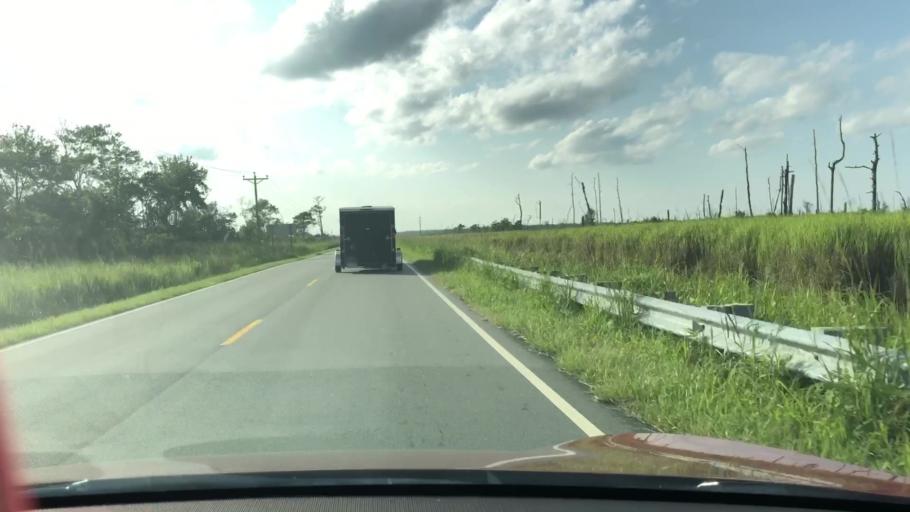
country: US
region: North Carolina
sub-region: Dare County
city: Wanchese
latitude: 35.6218
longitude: -75.8403
